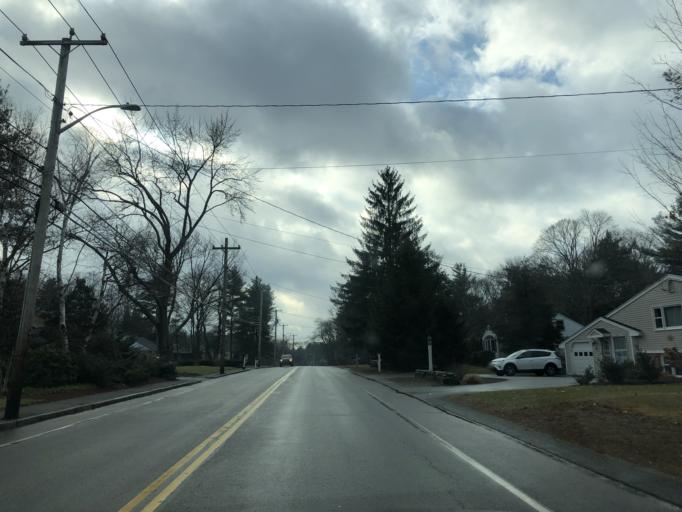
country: US
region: Massachusetts
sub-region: Norfolk County
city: Plainville
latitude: 41.9913
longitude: -71.2904
